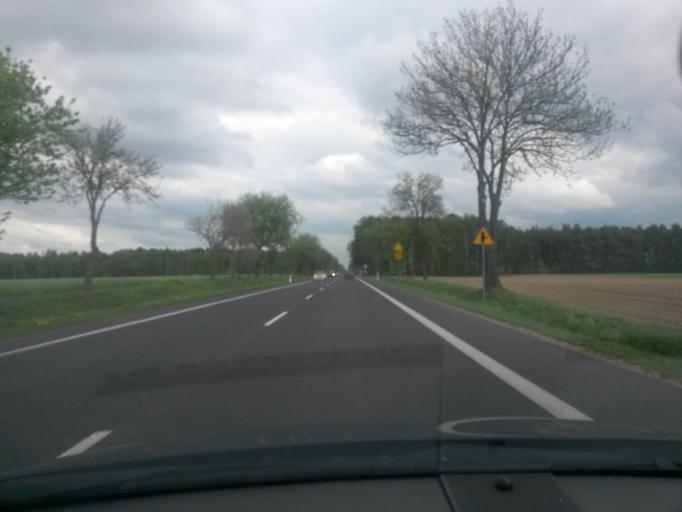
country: PL
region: Masovian Voivodeship
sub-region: Powiat sierpecki
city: Zawidz
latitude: 52.7836
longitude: 19.8964
